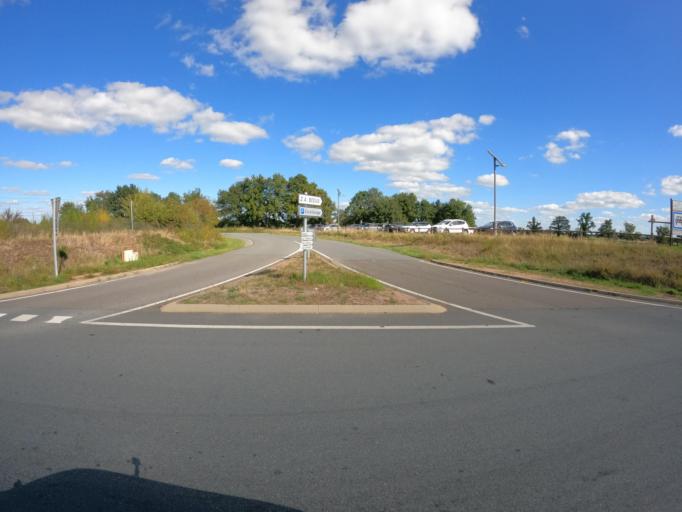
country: FR
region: Auvergne
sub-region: Departement de l'Allier
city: Desertines
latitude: 46.3870
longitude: 2.6975
